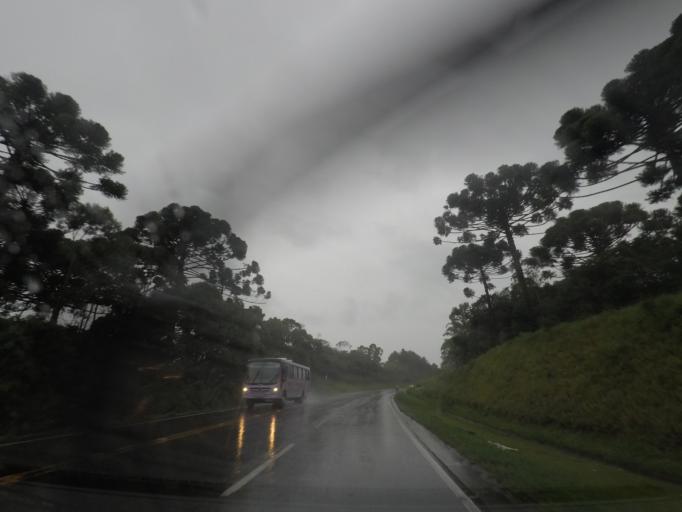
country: BR
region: Parana
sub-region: Almirante Tamandare
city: Almirante Tamandare
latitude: -25.3539
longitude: -49.3057
